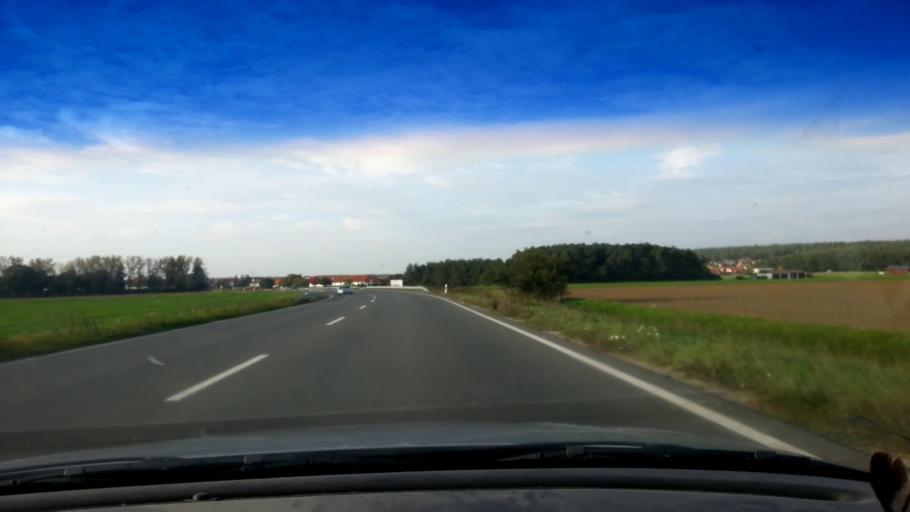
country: DE
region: Bavaria
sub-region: Upper Franconia
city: Strullendorf
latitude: 49.8362
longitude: 10.9769
